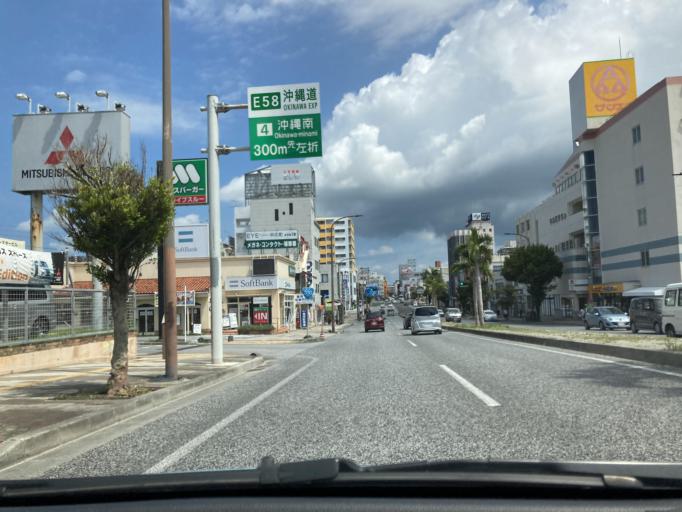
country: JP
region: Okinawa
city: Okinawa
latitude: 26.3330
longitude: 127.7984
